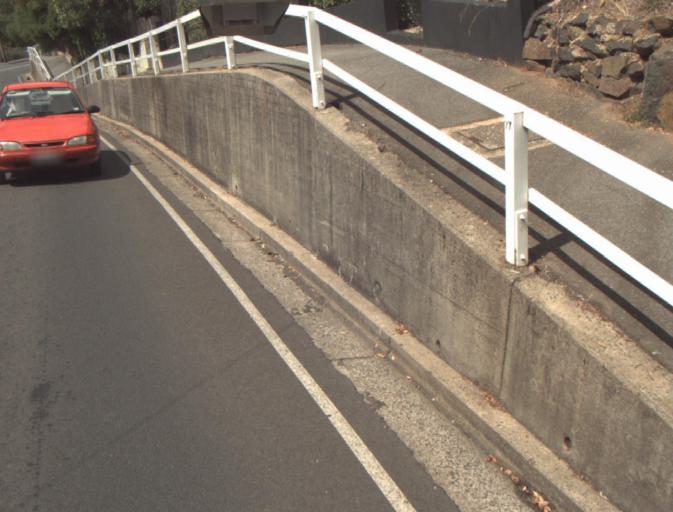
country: AU
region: Tasmania
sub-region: Launceston
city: Launceston
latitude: -41.4353
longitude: 147.1201
